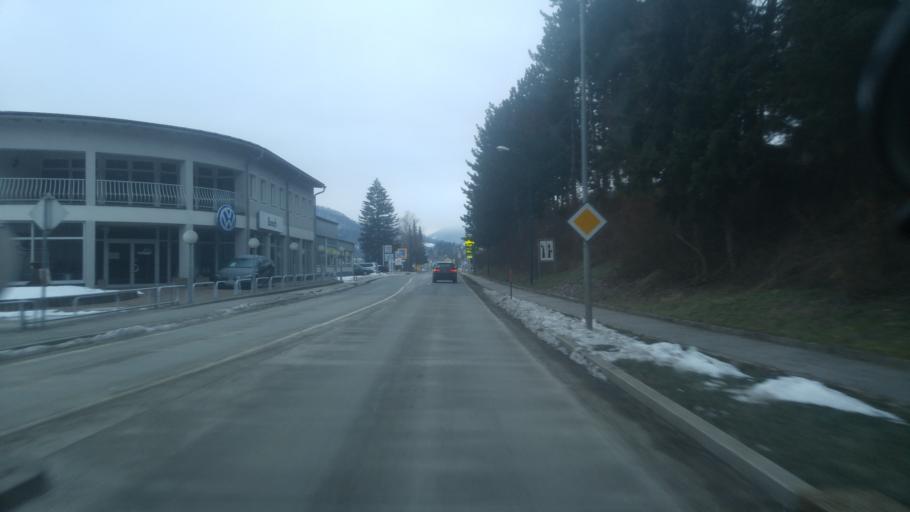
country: AT
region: Lower Austria
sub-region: Politischer Bezirk Lilienfeld
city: Traisen
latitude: 48.0500
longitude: 15.6105
